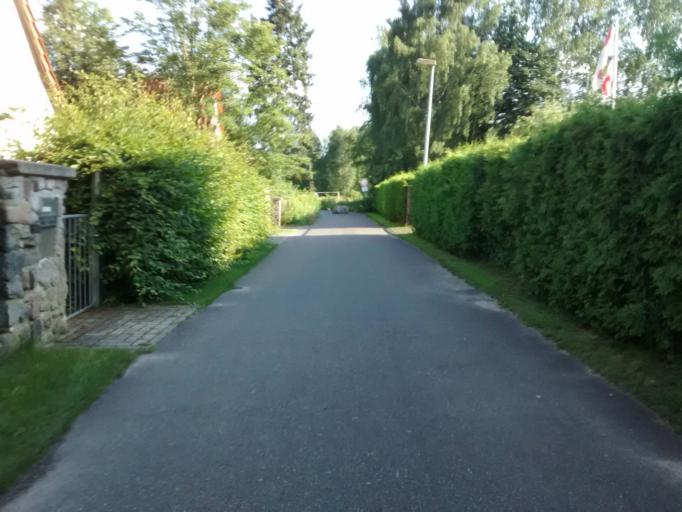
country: DE
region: Brandenburg
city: Hohen Neuendorf
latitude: 52.6576
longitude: 13.2815
